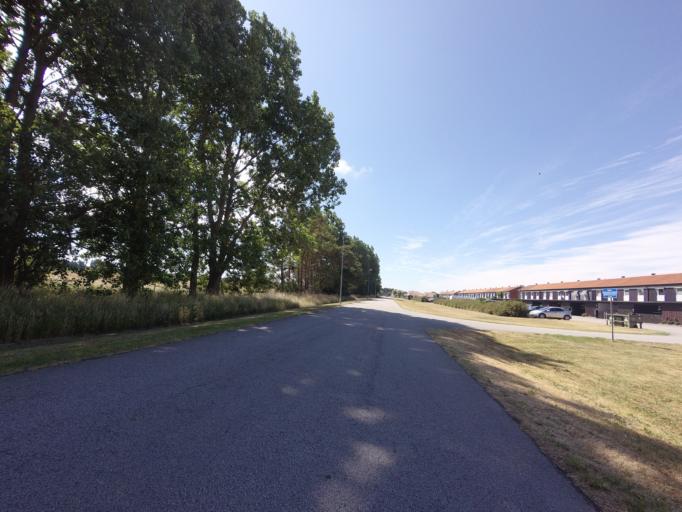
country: SE
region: Skane
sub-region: Vellinge Kommun
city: Skanor med Falsterbo
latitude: 55.4184
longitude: 12.8628
